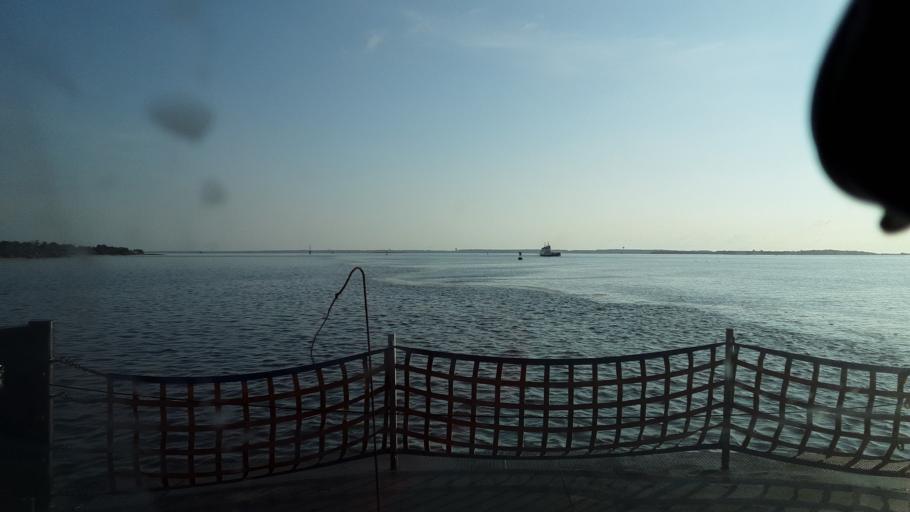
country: US
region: North Carolina
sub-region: Brunswick County
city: Southport
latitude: 33.9522
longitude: -77.9626
